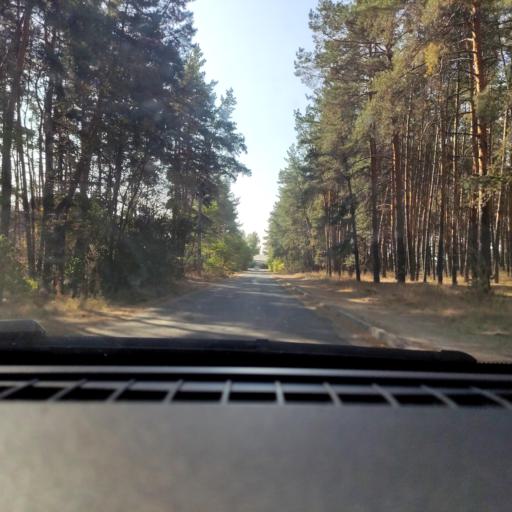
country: RU
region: Voronezj
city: Maslovka
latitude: 51.5485
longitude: 39.2213
